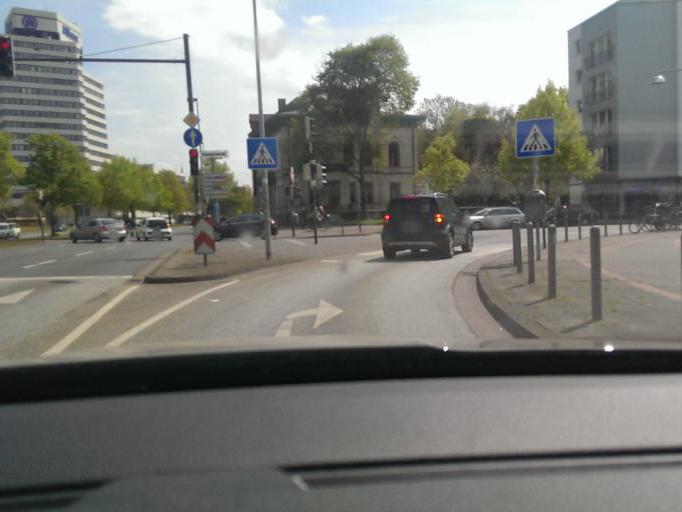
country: DE
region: Lower Saxony
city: Hannover
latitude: 52.3780
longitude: 9.7229
